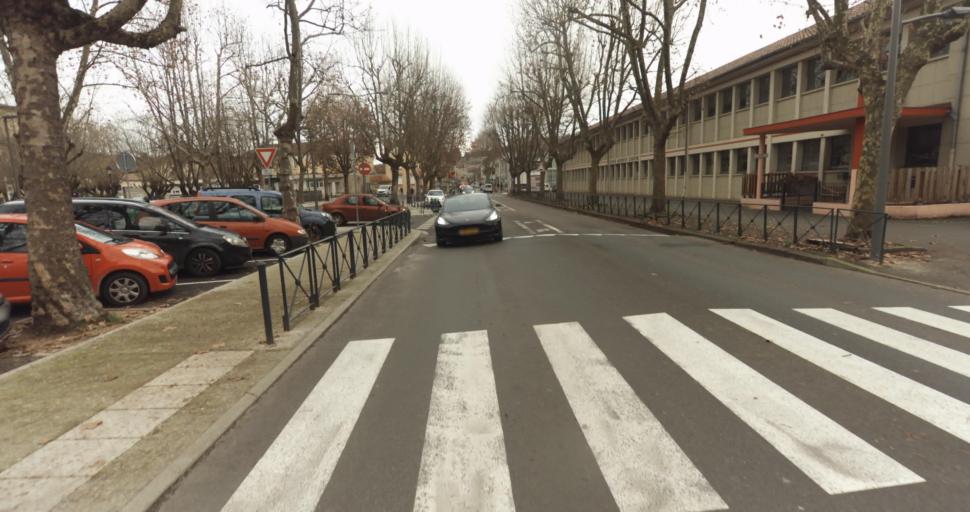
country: FR
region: Midi-Pyrenees
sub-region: Departement du Lot
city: Figeac
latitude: 44.6091
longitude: 2.0284
